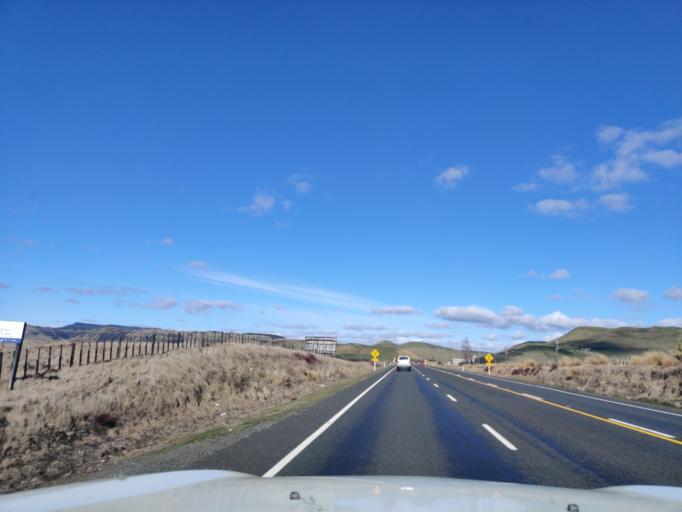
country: NZ
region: Manawatu-Wanganui
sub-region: Ruapehu District
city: Waiouru
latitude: -39.4923
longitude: 175.6716
